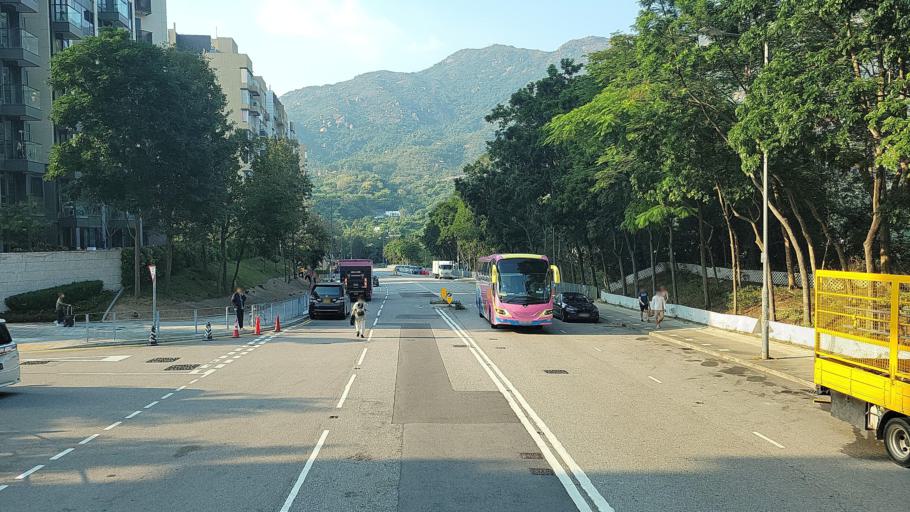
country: HK
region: Tuen Mun
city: Tuen Mun
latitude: 22.3737
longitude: 114.0028
